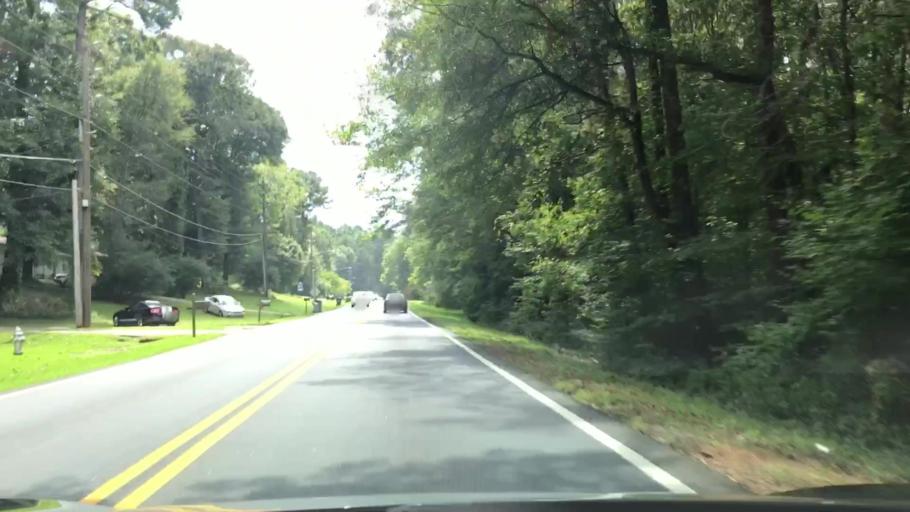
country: US
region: Georgia
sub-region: Gwinnett County
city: Snellville
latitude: 33.9002
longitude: -84.0678
